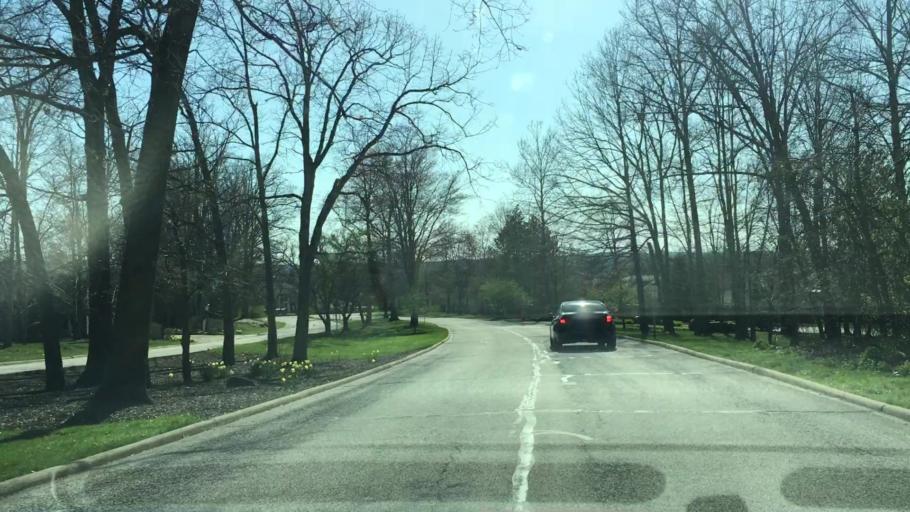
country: US
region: Ohio
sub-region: Summit County
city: Northfield
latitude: 41.3122
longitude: -81.5677
